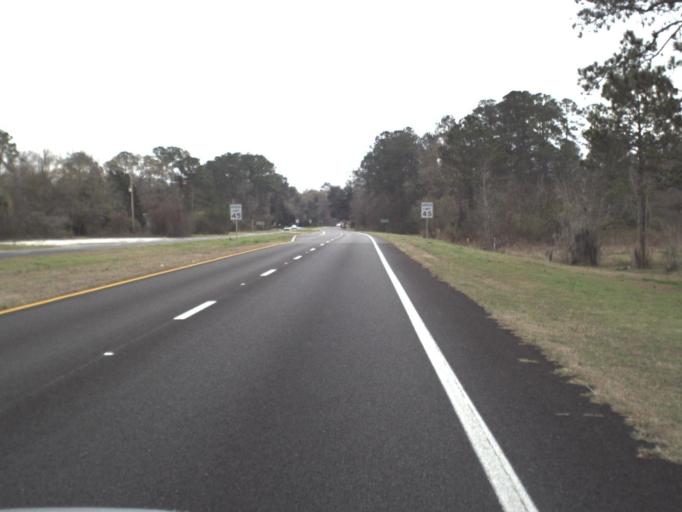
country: US
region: Florida
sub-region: Jefferson County
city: Monticello
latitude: 30.3801
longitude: -83.8190
